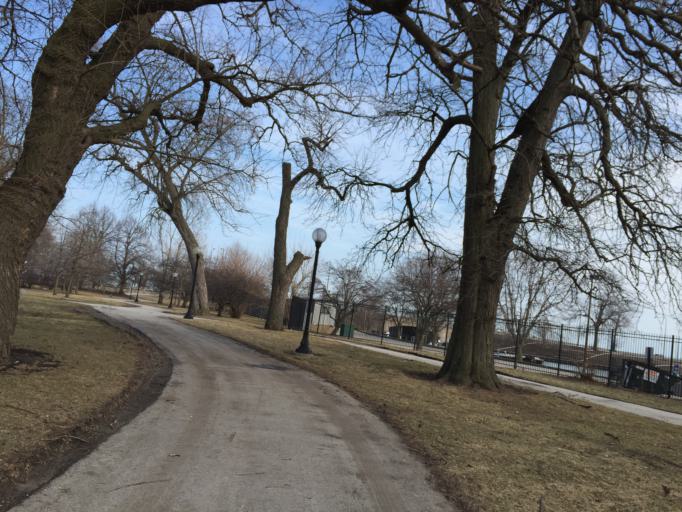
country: US
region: Illinois
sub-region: Cook County
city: Chicago
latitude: 41.7887
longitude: -87.5797
